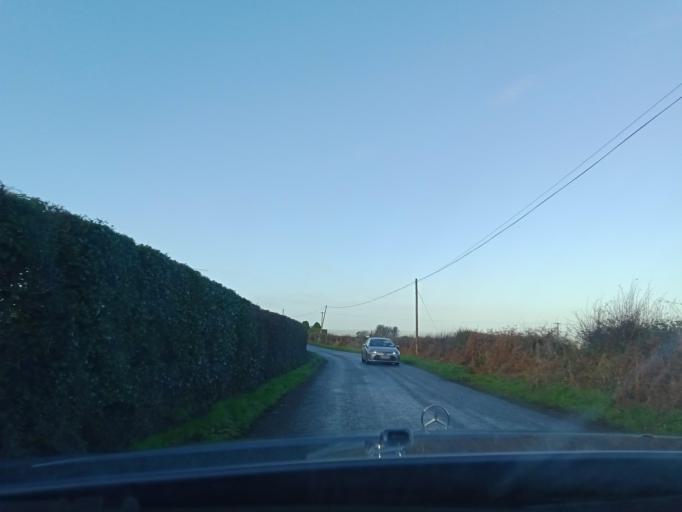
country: IE
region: Leinster
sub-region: Kilkenny
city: Callan
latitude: 52.4734
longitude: -7.4255
